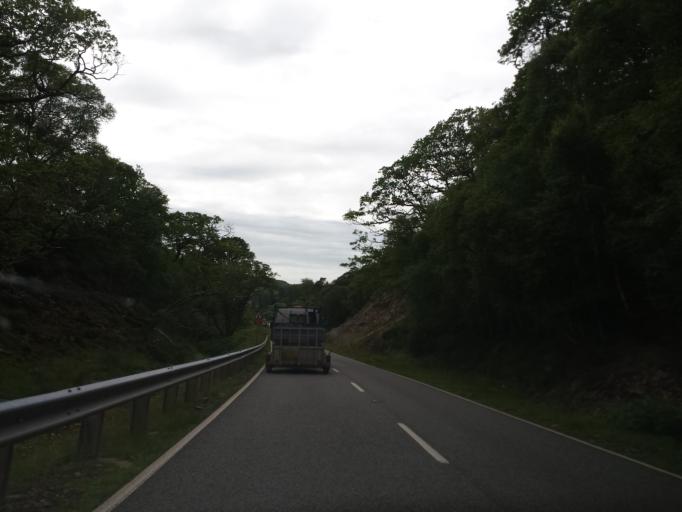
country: GB
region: Scotland
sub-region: Argyll and Bute
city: Isle Of Mull
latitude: 56.8996
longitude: -5.7732
